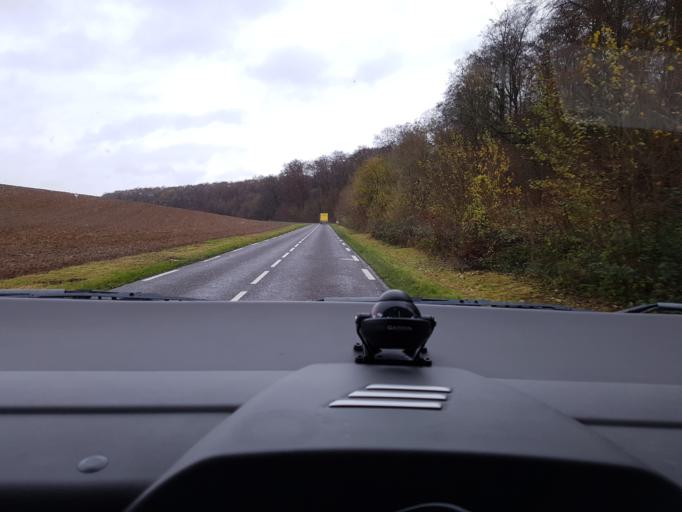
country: FR
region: Haute-Normandie
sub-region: Departement de la Seine-Maritime
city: Gournay-en-Bray
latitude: 49.4190
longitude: 1.6373
